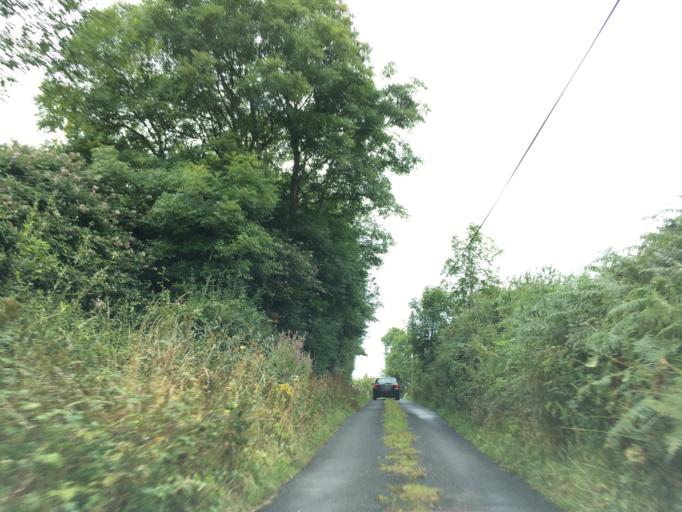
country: IE
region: Munster
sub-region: An Clar
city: Ennis
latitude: 52.7280
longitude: -9.0755
